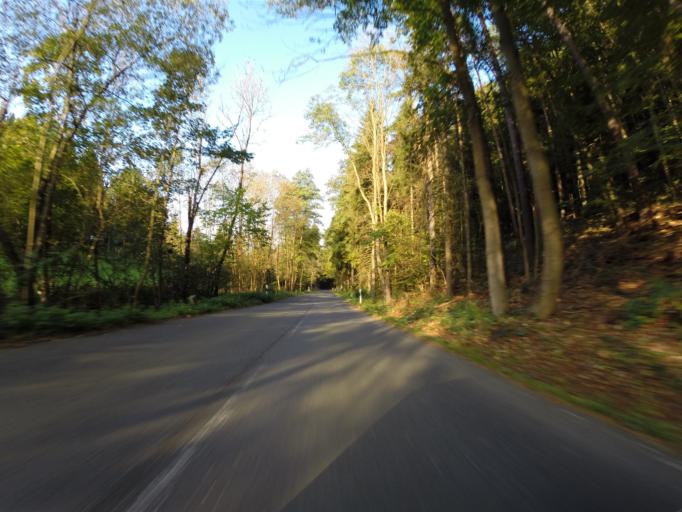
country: DE
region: Thuringia
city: Bucha
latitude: 50.9285
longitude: 11.5348
